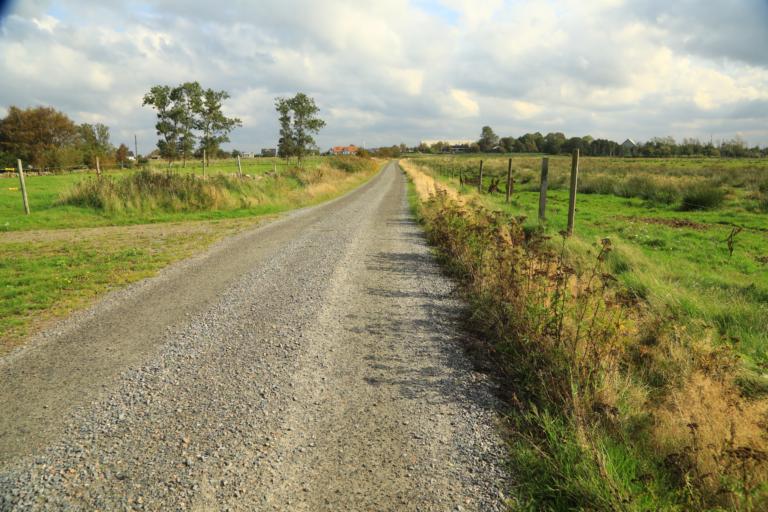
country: SE
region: Halland
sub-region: Varbergs Kommun
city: Traslovslage
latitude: 57.0266
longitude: 12.3272
